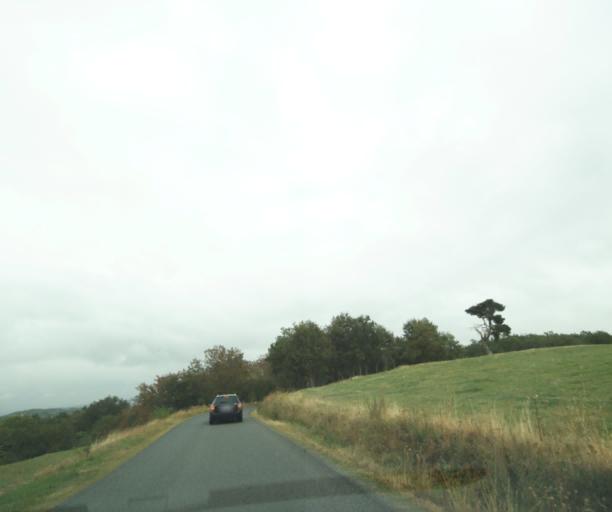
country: FR
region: Auvergne
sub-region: Departement du Puy-de-Dome
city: Orcines
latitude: 45.8026
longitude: 3.0267
